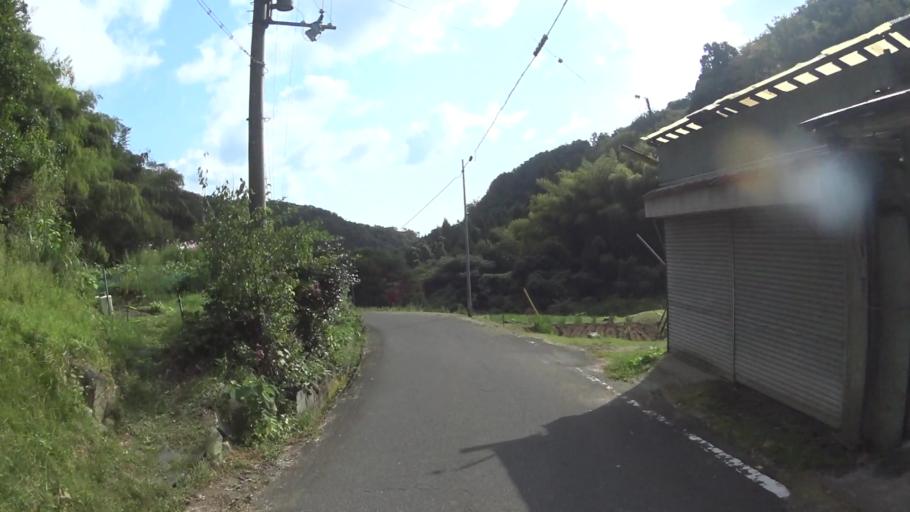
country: JP
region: Kyoto
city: Miyazu
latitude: 35.6110
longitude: 135.1984
